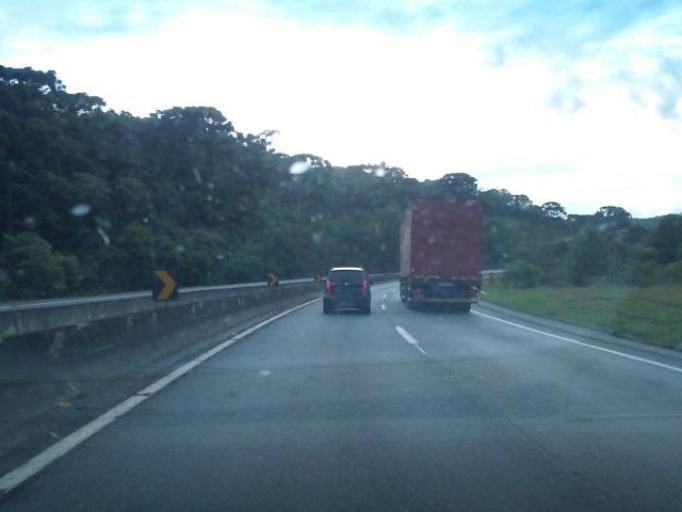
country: BR
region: Parana
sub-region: Campina Grande Do Sul
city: Campina Grande do Sul
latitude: -25.3108
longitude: -49.0031
